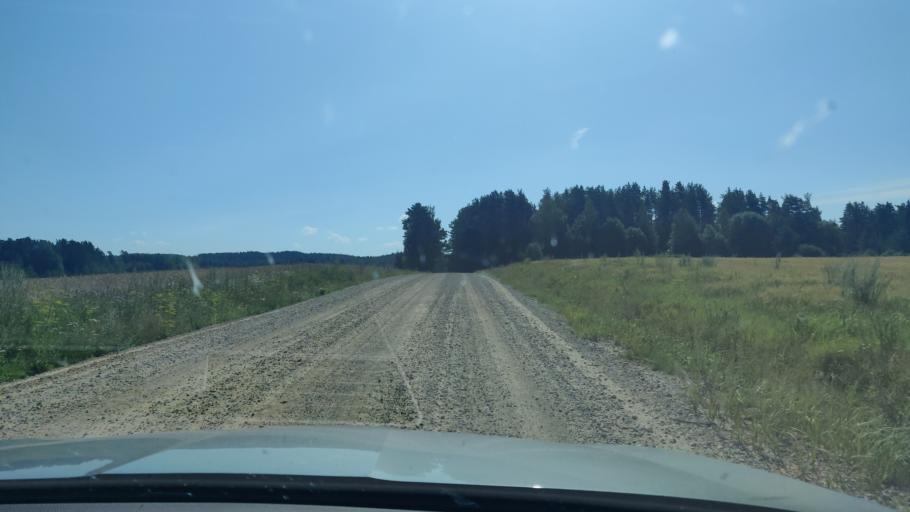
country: EE
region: Tartu
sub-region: Elva linn
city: Elva
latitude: 58.1350
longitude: 26.3980
